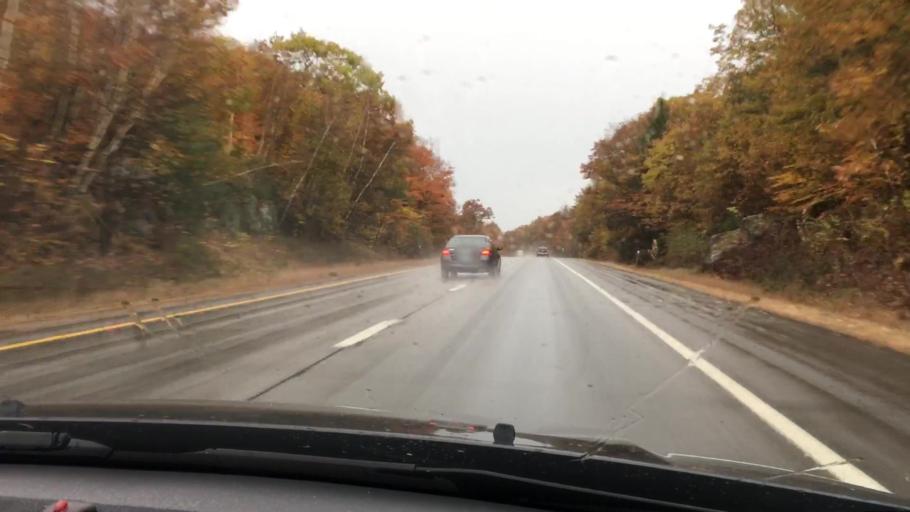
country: US
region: New Hampshire
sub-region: Belknap County
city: Sanbornton
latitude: 43.5507
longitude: -71.6173
